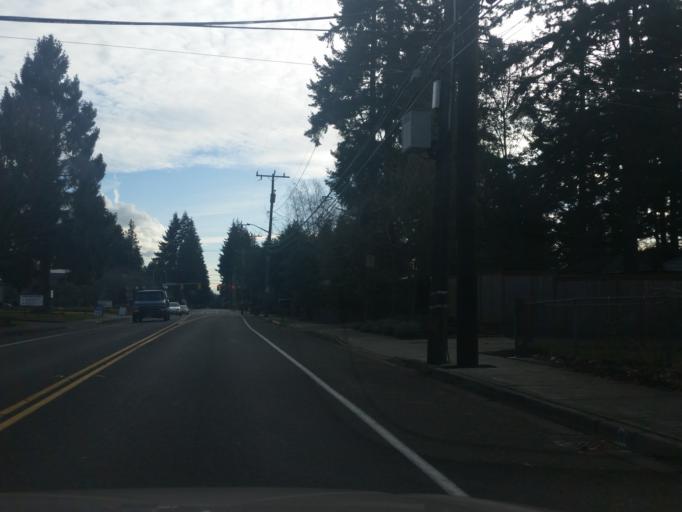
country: US
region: Washington
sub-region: King County
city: Shoreline
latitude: 47.7648
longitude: -122.3297
